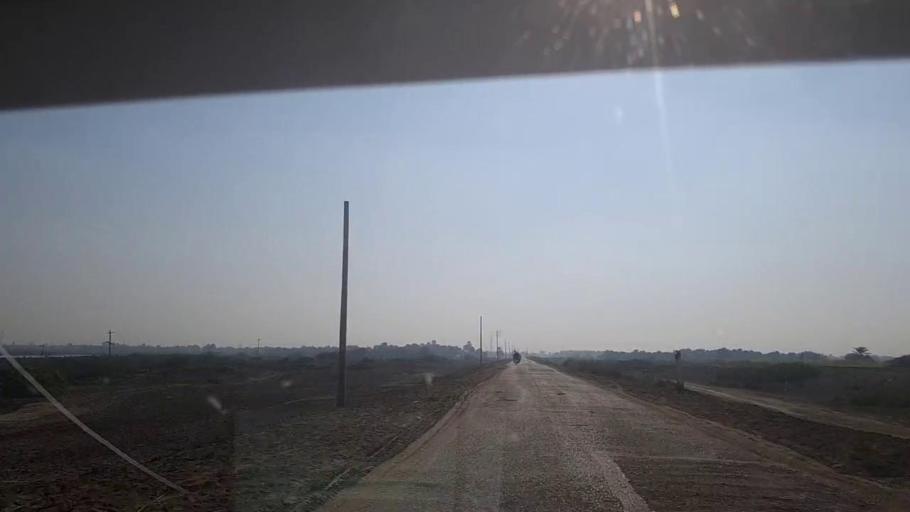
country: PK
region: Sindh
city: Gambat
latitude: 27.3560
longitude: 68.5528
